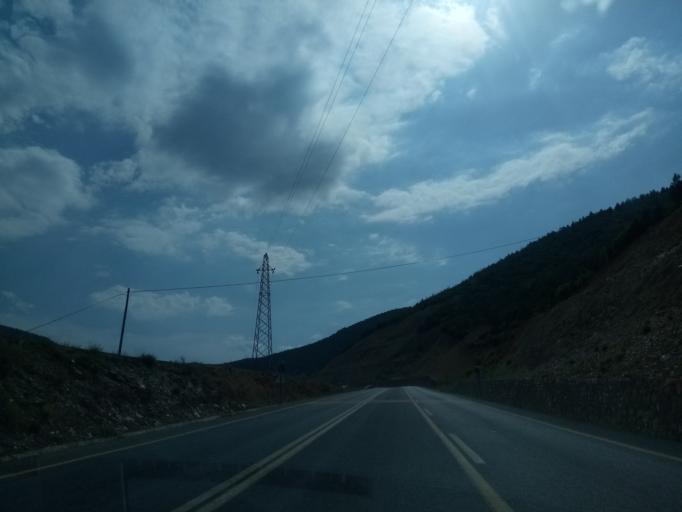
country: TR
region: Konya
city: Aksehir
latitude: 38.3015
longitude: 31.4563
